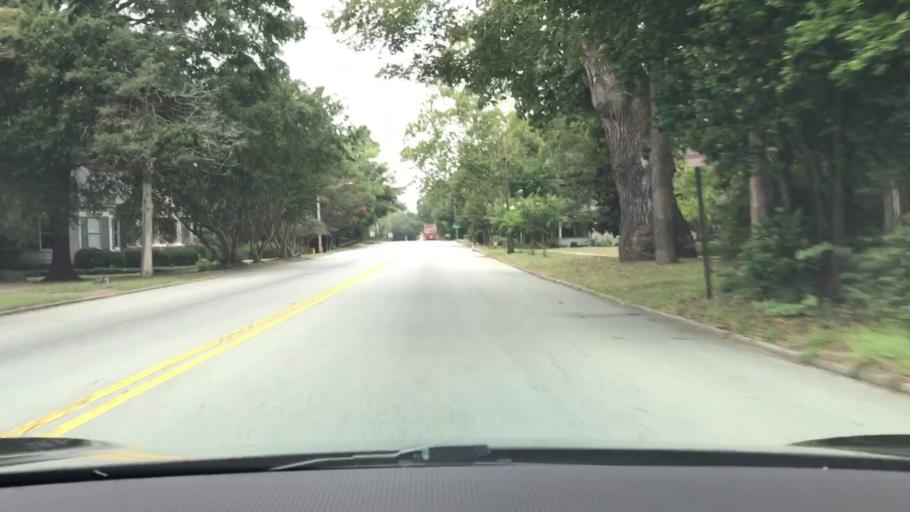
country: US
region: Georgia
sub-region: Greene County
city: Greensboro
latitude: 33.5761
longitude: -83.1847
